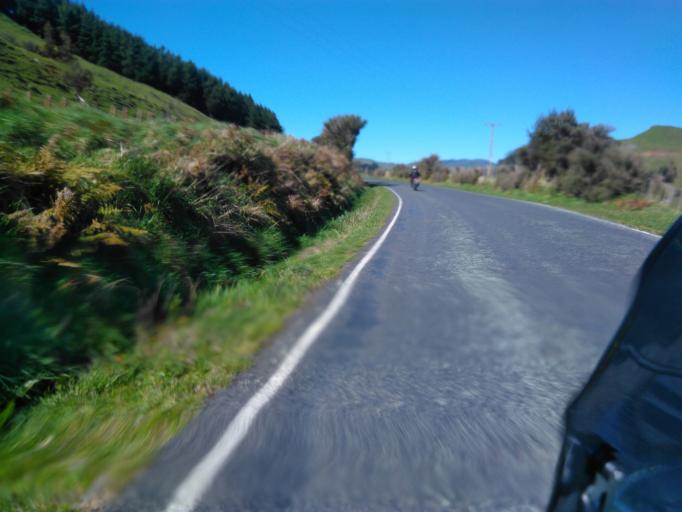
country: NZ
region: Bay of Plenty
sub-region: Opotiki District
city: Opotiki
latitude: -38.3250
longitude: 177.5306
